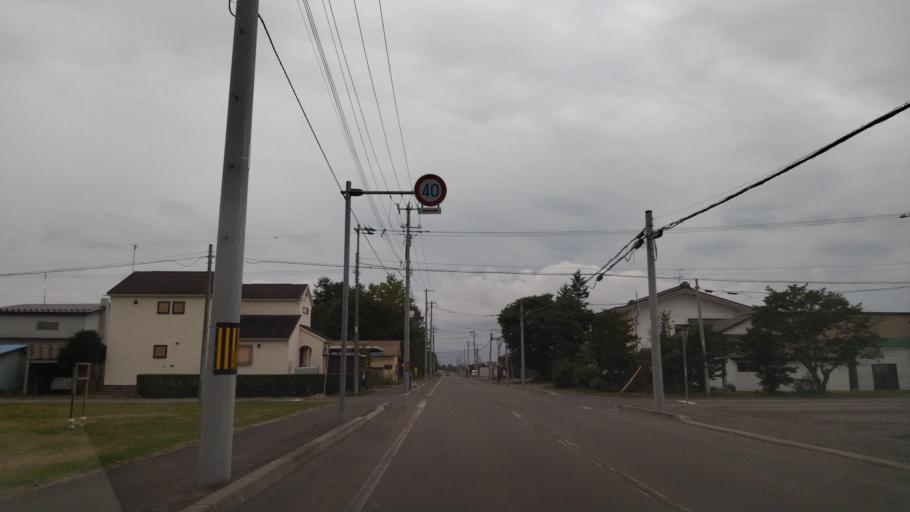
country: JP
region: Hokkaido
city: Otofuke
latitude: 43.2294
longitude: 143.2914
